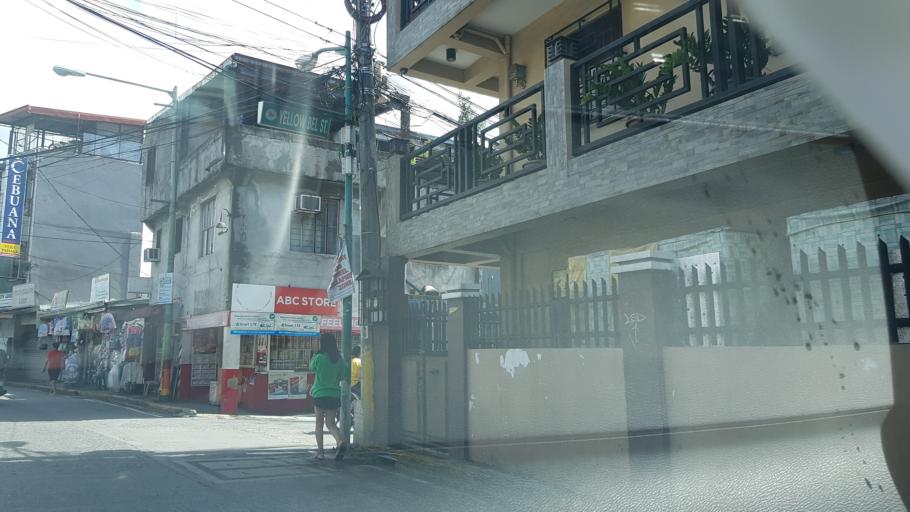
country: PH
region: Calabarzon
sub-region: Province of Rizal
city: Pateros
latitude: 14.5416
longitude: 121.0598
